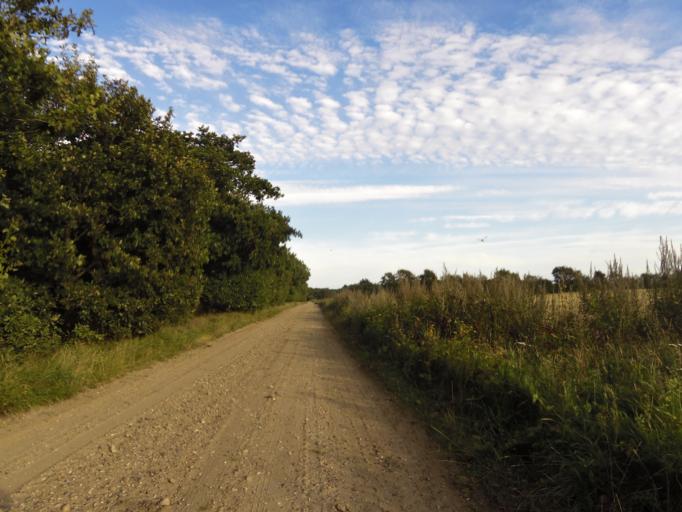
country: DK
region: South Denmark
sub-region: Haderslev Kommune
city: Gram
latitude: 55.3124
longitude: 8.9126
